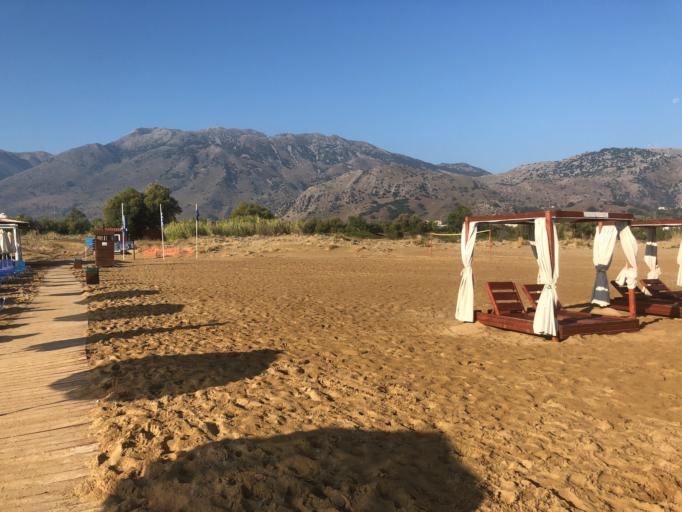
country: GR
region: Crete
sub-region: Nomos Chanias
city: Georgioupolis
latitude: 35.3554
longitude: 24.2862
